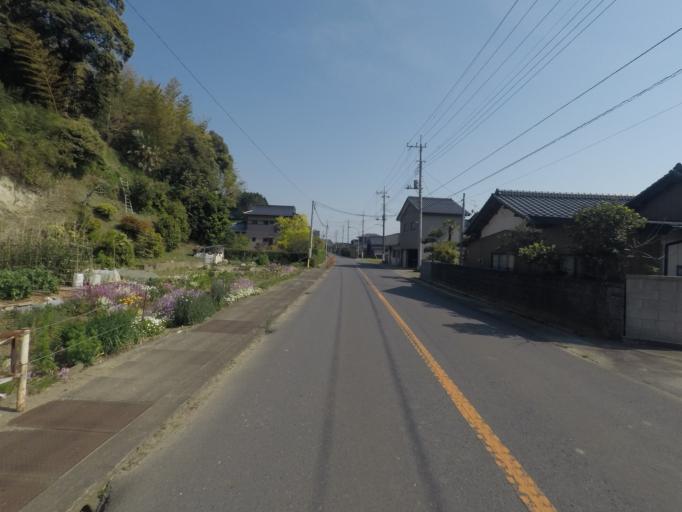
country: JP
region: Ibaraki
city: Inashiki
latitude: 36.0693
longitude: 140.4300
